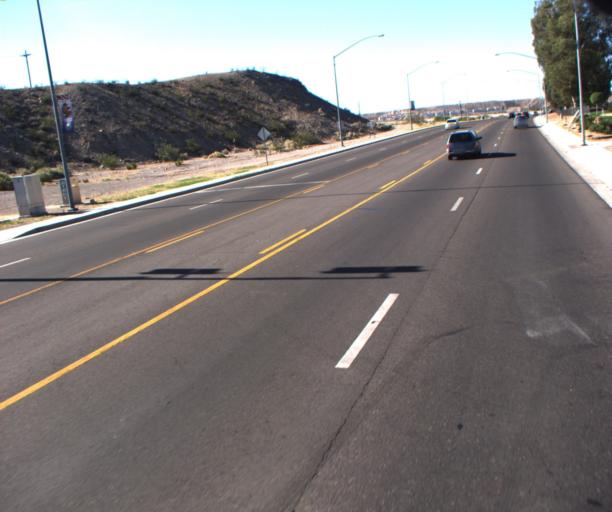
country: US
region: Arizona
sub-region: Mohave County
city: Bullhead City
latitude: 35.1413
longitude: -114.5695
